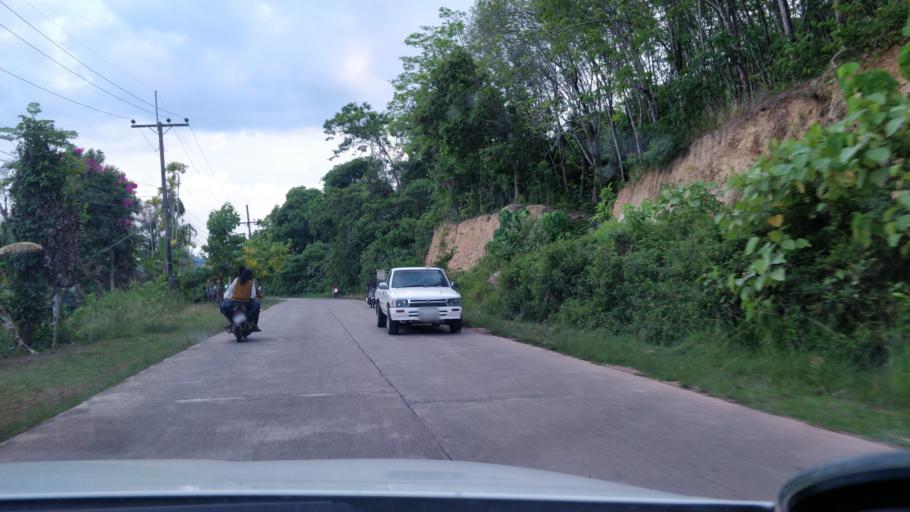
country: TH
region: Krabi
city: Ko Lanta
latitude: 7.5778
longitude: 99.0684
